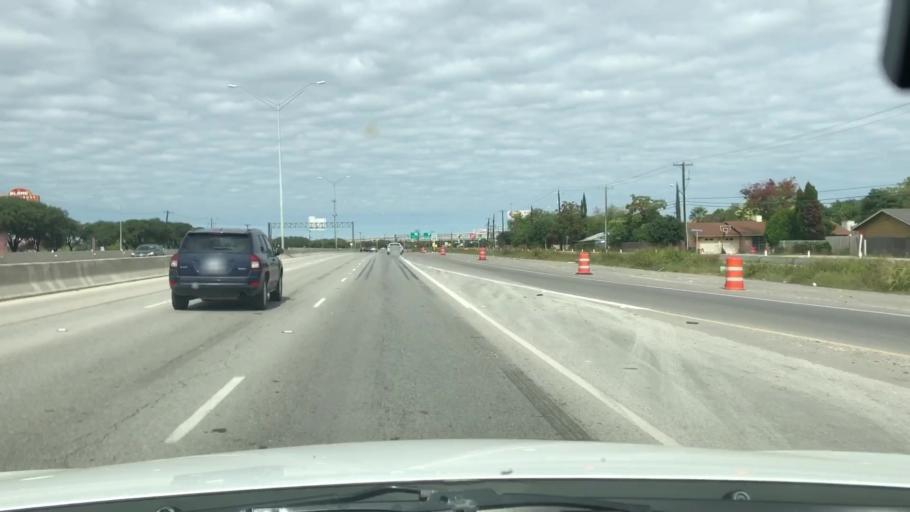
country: US
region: Texas
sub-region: Bexar County
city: Lackland Air Force Base
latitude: 29.4242
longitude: -98.6495
